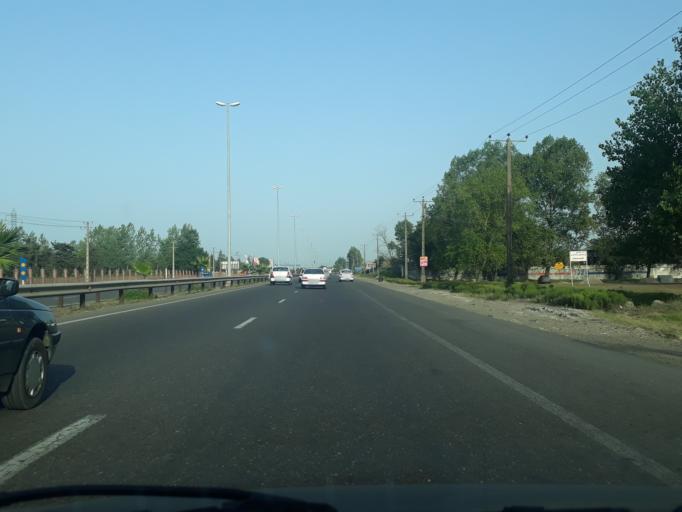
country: IR
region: Gilan
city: Bandar-e Anzali
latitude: 37.4605
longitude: 49.5750
